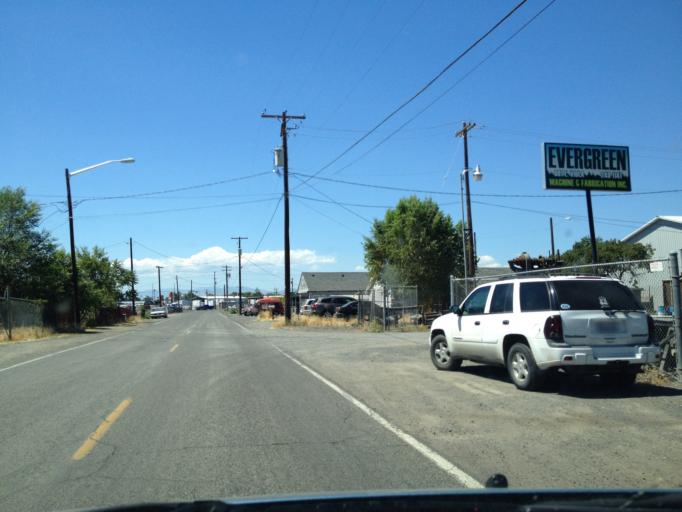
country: US
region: Washington
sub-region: Yakima County
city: Yakima
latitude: 46.5814
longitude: -120.4907
